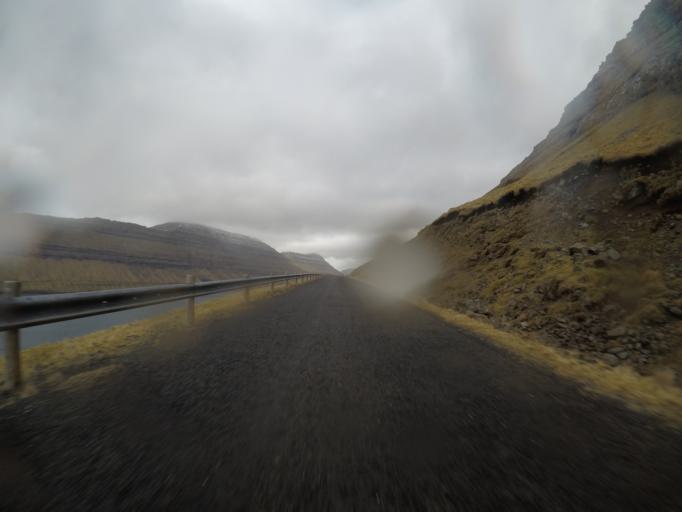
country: FO
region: Nordoyar
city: Klaksvik
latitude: 62.3307
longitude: -6.5723
